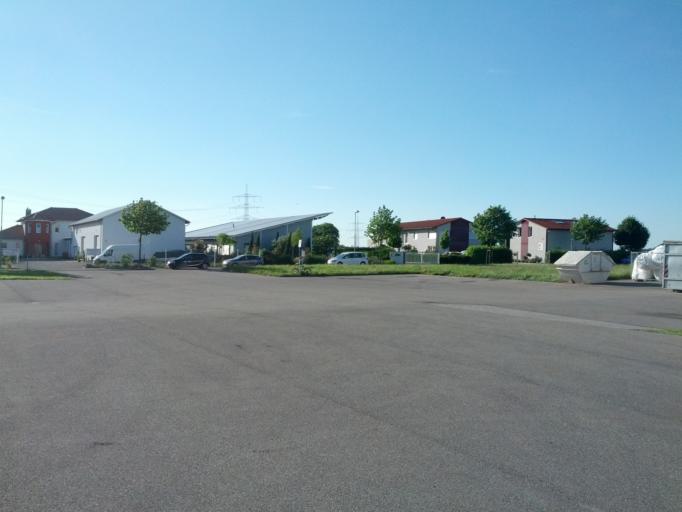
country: DE
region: Baden-Wuerttemberg
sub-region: Freiburg Region
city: Pfaffenweiler
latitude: 47.9236
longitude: 7.7272
